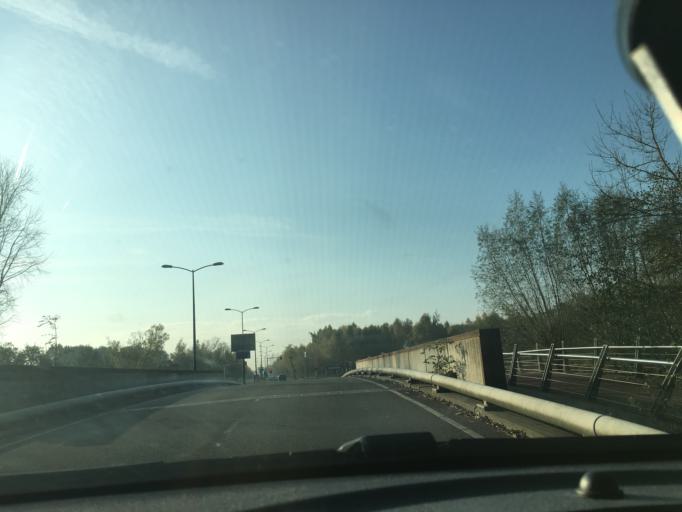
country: NL
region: North Brabant
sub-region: Gemeente Eindhoven
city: Eindhoven
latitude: 51.4163
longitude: 5.4647
